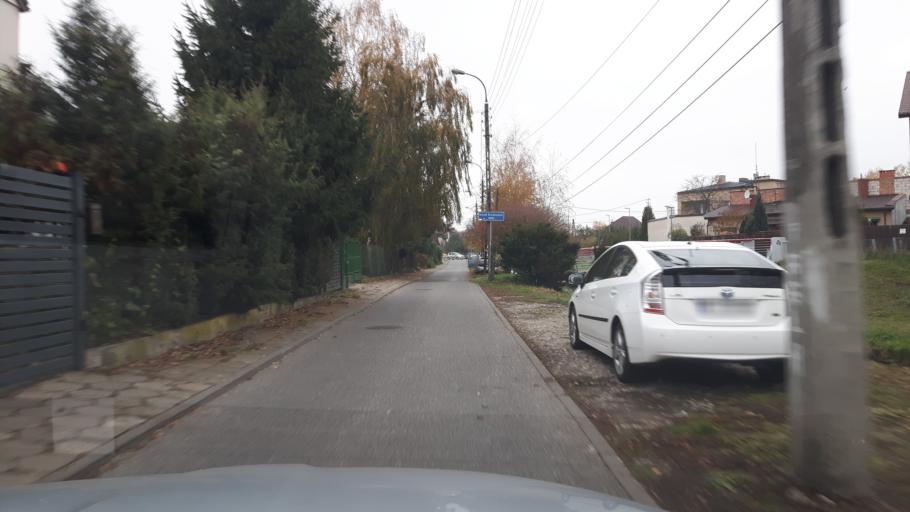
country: PL
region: Masovian Voivodeship
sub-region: Warszawa
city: Targowek
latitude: 52.2801
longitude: 21.0637
